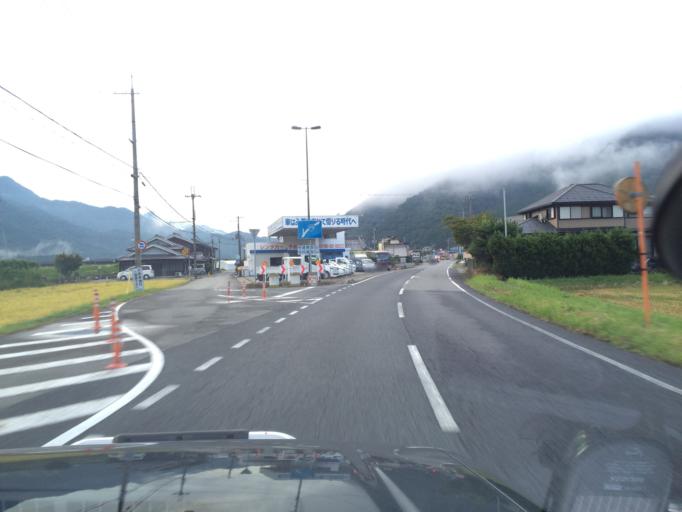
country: JP
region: Hyogo
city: Nishiwaki
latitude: 35.1191
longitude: 135.0037
